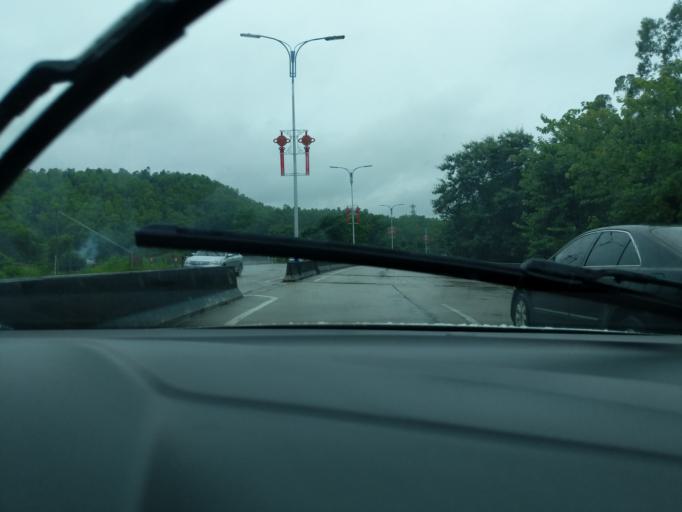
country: CN
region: Guangdong
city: Pingshi
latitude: 22.2282
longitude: 112.3119
